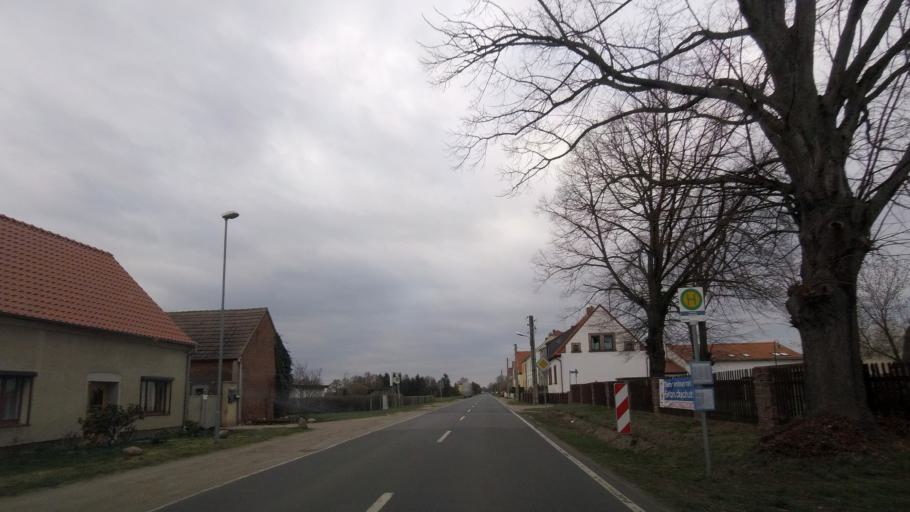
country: DE
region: Saxony-Anhalt
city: Kemberg
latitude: 51.7792
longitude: 12.6274
